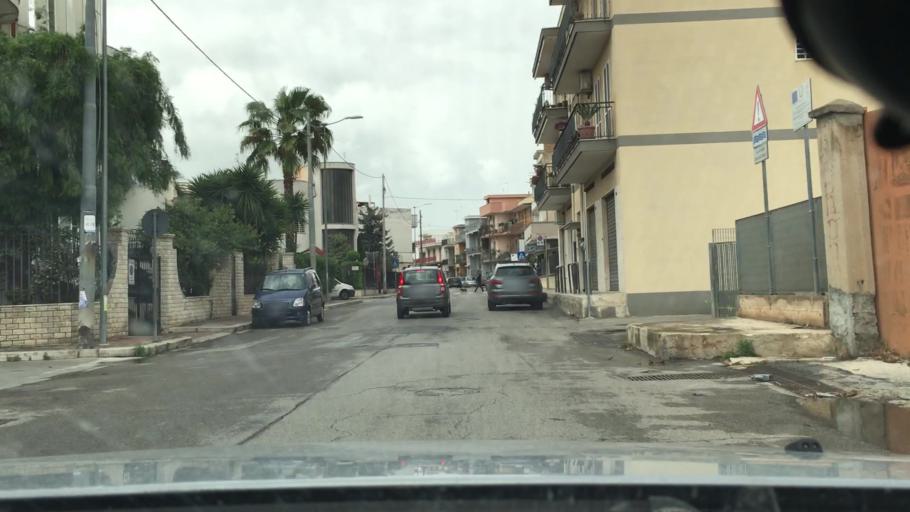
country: IT
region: Apulia
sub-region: Provincia di Bari
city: Capurso
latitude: 41.0464
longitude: 16.9282
